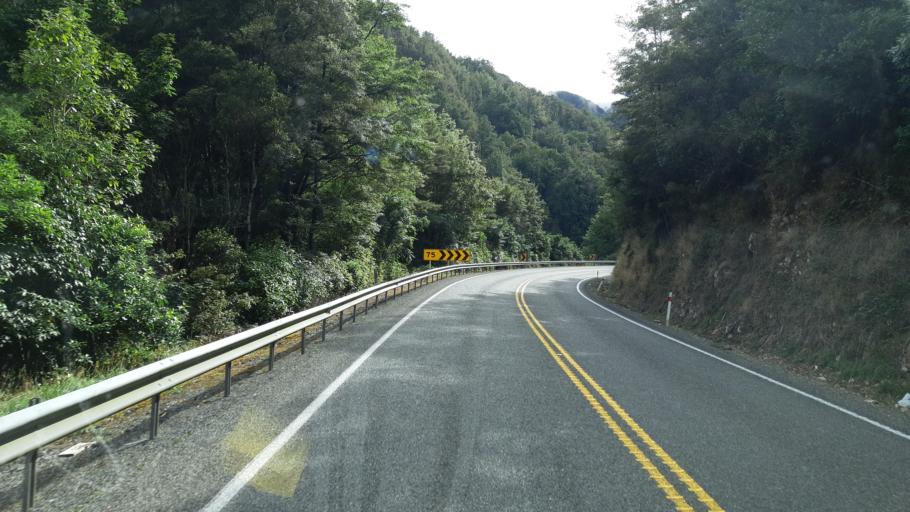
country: NZ
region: West Coast
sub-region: Buller District
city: Westport
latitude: -41.7701
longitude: 172.2300
